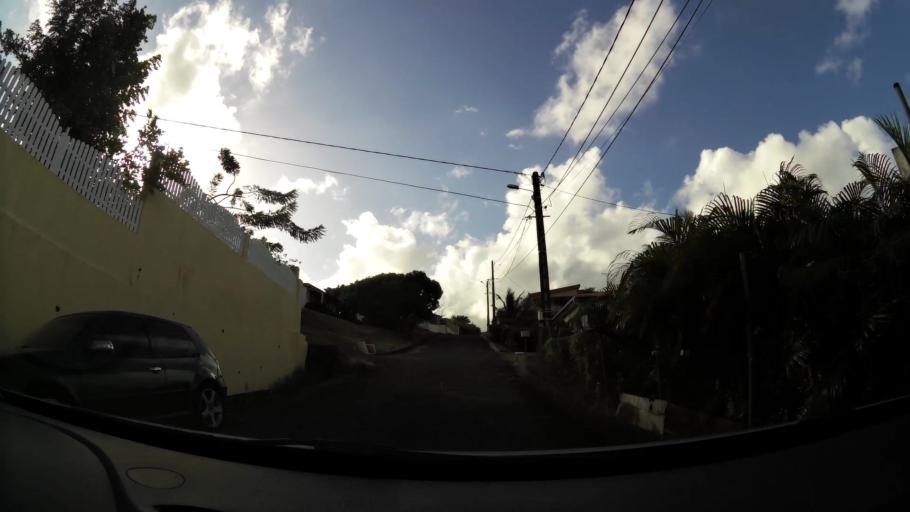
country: MQ
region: Martinique
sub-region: Martinique
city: Le Francois
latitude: 14.6132
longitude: -60.9108
